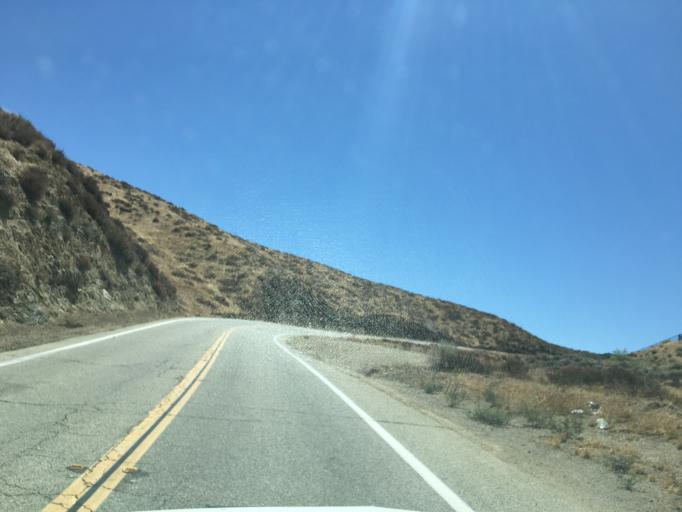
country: US
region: California
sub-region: Los Angeles County
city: Leona Valley
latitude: 34.6103
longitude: -118.2469
